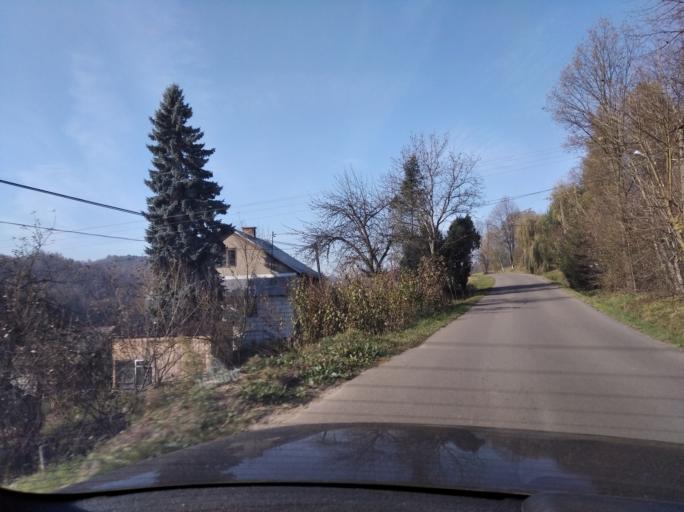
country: PL
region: Subcarpathian Voivodeship
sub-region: Powiat strzyzowski
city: Wisniowa
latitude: 49.8729
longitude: 21.6270
